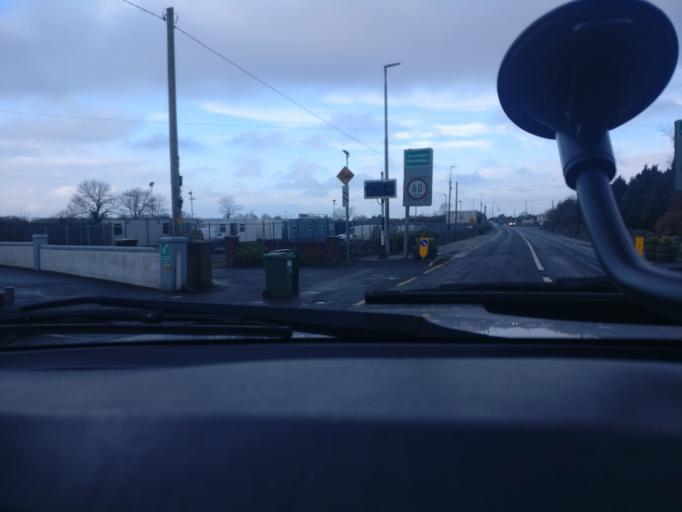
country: IE
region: Connaught
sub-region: County Galway
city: Athenry
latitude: 53.2332
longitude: -8.7398
